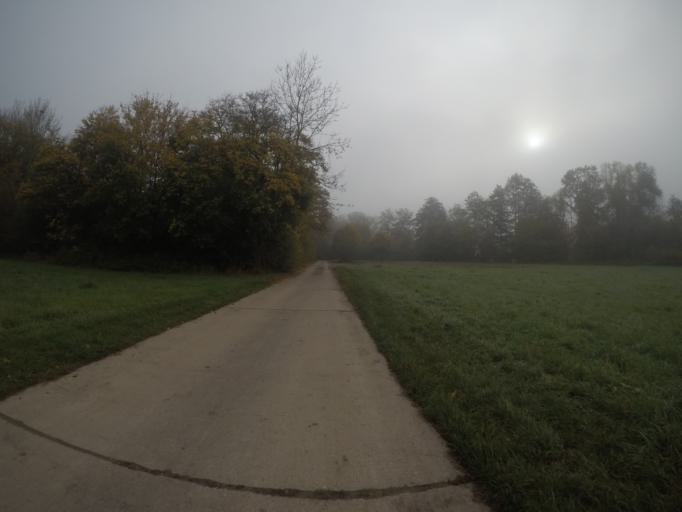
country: DE
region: Baden-Wuerttemberg
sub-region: Regierungsbezirk Stuttgart
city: Neuhausen auf den Fildern
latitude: 48.7052
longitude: 9.2747
